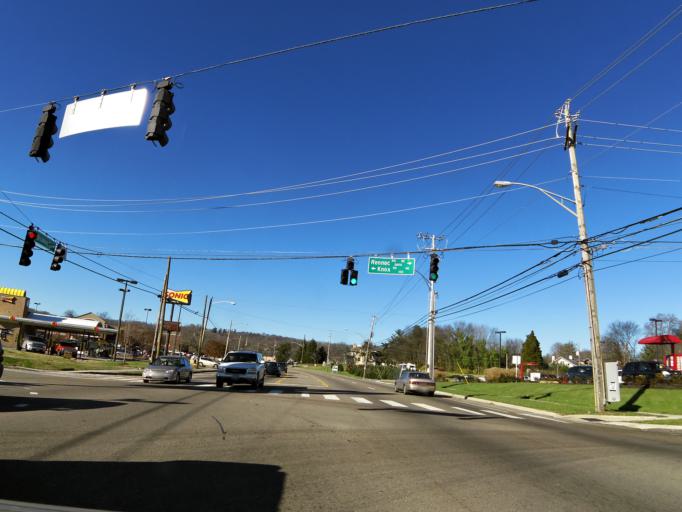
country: US
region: Tennessee
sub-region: Knox County
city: Knoxville
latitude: 36.0315
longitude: -83.9297
